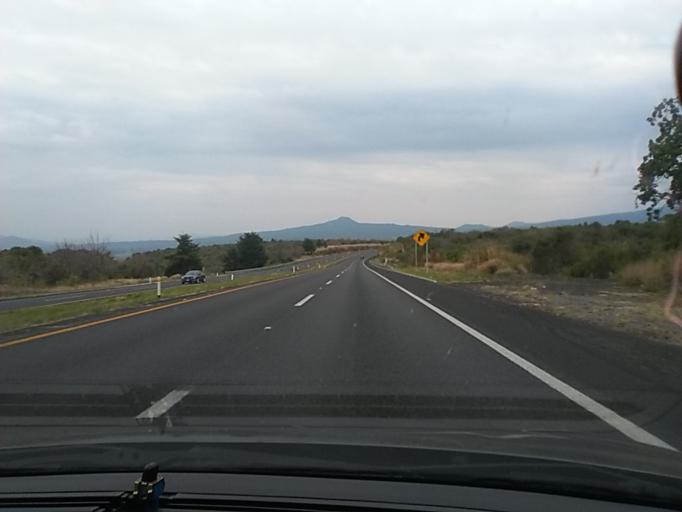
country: MX
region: Michoacan
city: Penjamillo de Degollado
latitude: 20.0750
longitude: -101.9724
